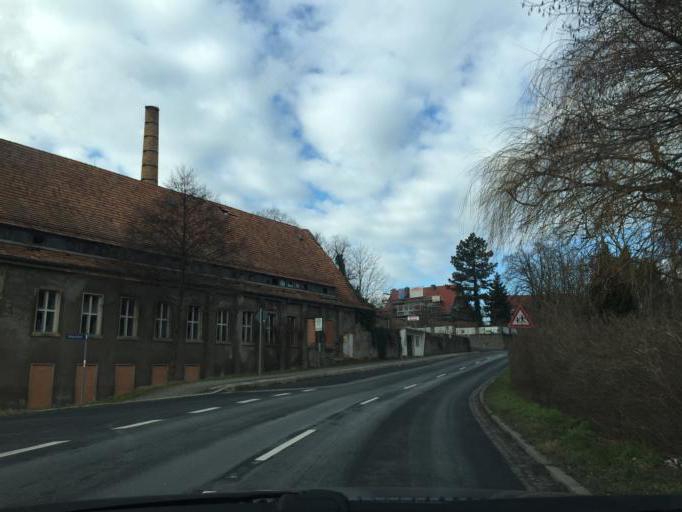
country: DE
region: Saxony
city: Ottendorf-Okrilla
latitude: 51.1823
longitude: 13.7916
